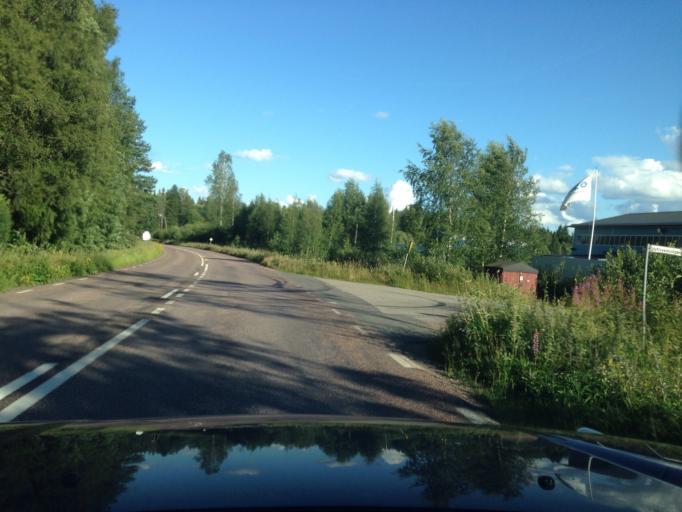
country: SE
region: Dalarna
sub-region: Ludvika Kommun
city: Ludvika
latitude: 60.1456
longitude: 15.1049
